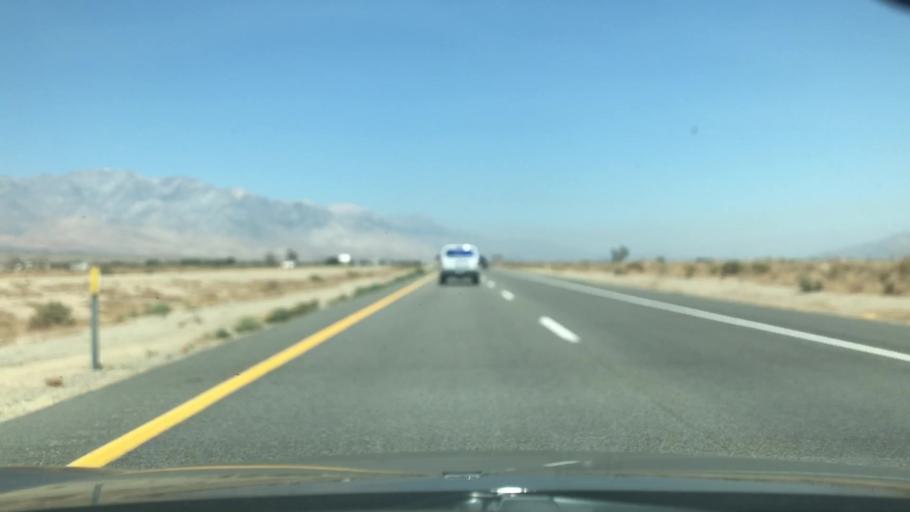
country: US
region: California
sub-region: Inyo County
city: Lone Pine
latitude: 36.7264
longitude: -118.1429
